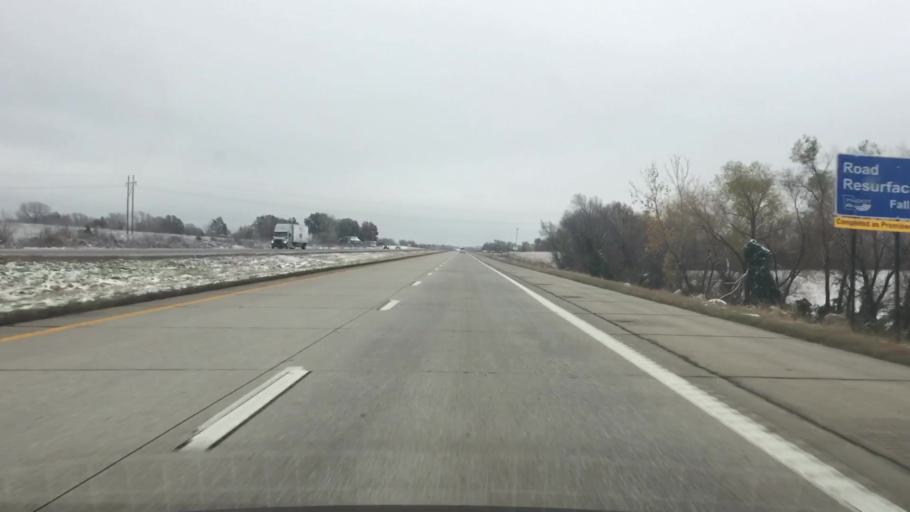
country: US
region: Missouri
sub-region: Saint Clair County
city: Osceola
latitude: 38.1874
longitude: -93.7372
